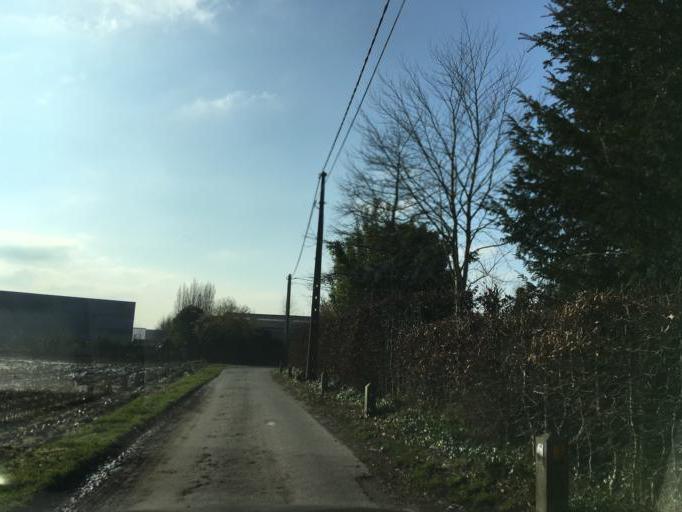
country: BE
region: Flanders
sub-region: Provincie West-Vlaanderen
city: Roeselare
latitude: 50.9485
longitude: 3.1608
